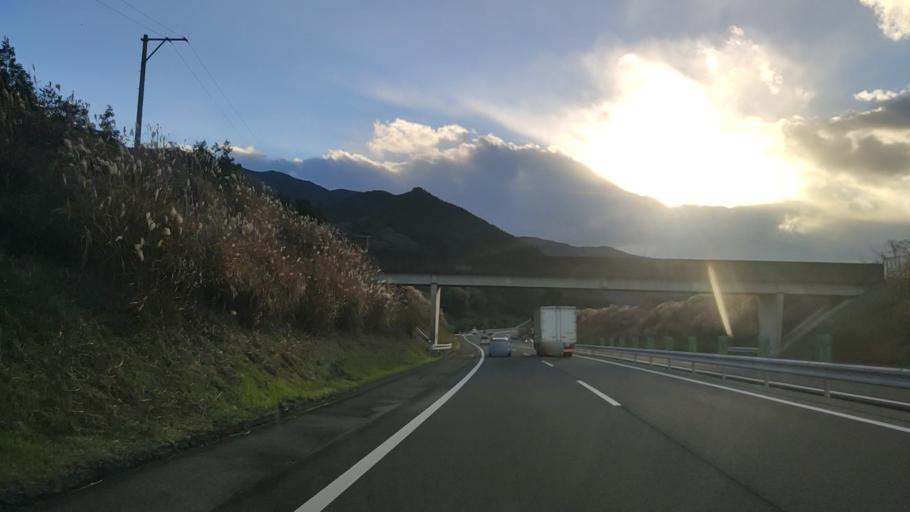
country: JP
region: Ehime
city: Saijo
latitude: 33.8687
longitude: 133.0594
